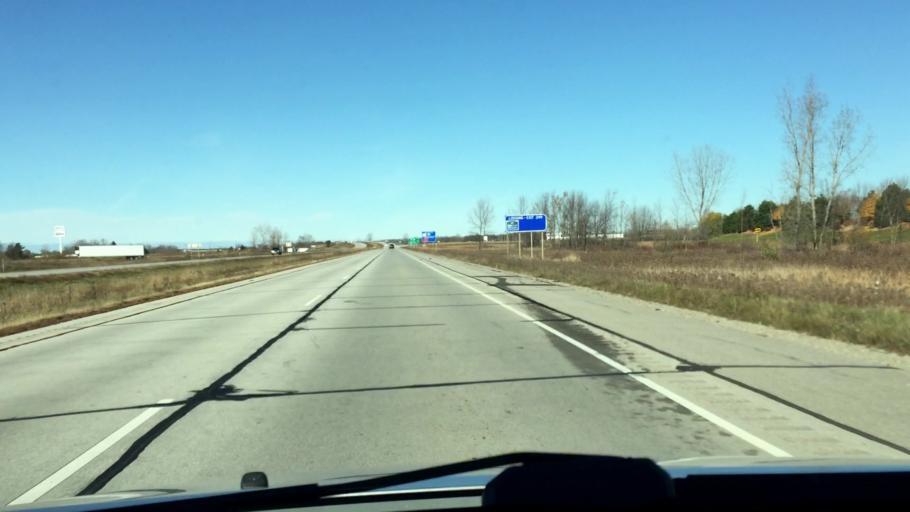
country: US
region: Wisconsin
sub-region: Brown County
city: Pulaski
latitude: 44.5923
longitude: -88.2076
